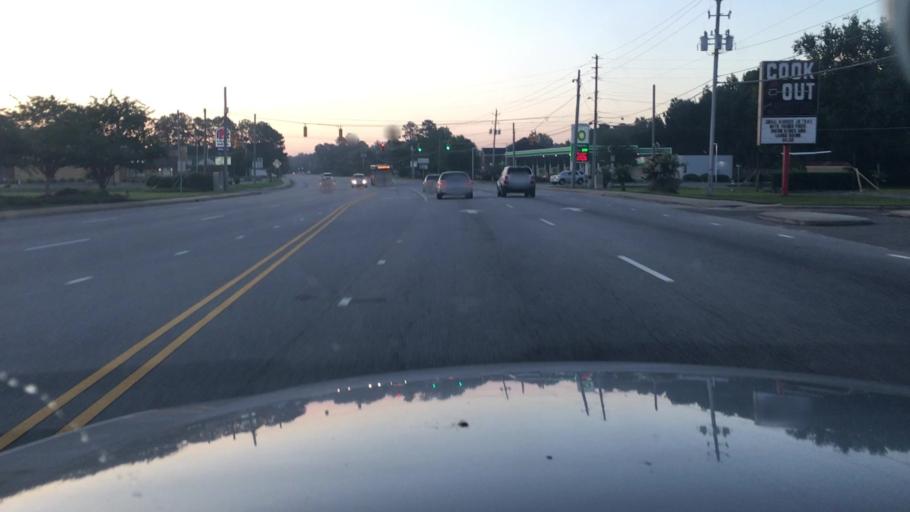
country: US
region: North Carolina
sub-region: Cumberland County
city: Fort Bragg
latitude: 35.0604
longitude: -79.0133
